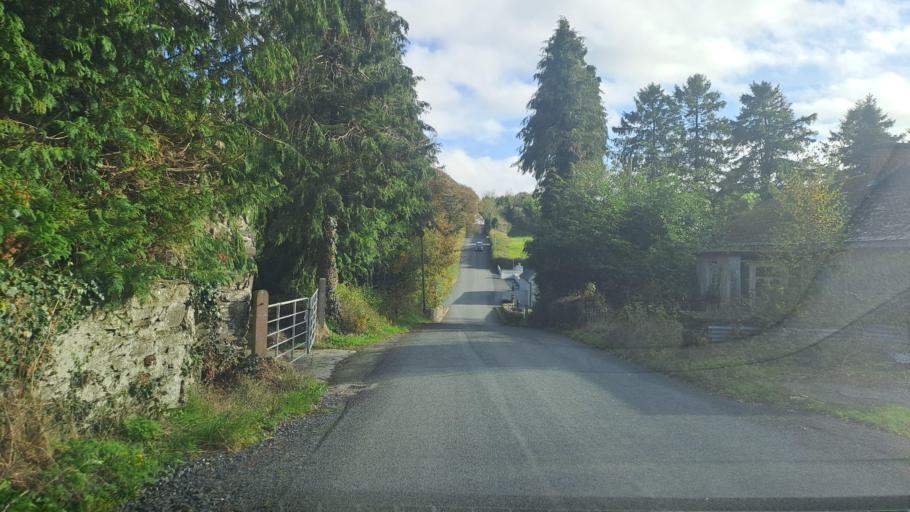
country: IE
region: Ulster
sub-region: An Cabhan
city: Bailieborough
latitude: 53.9934
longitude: -7.0246
